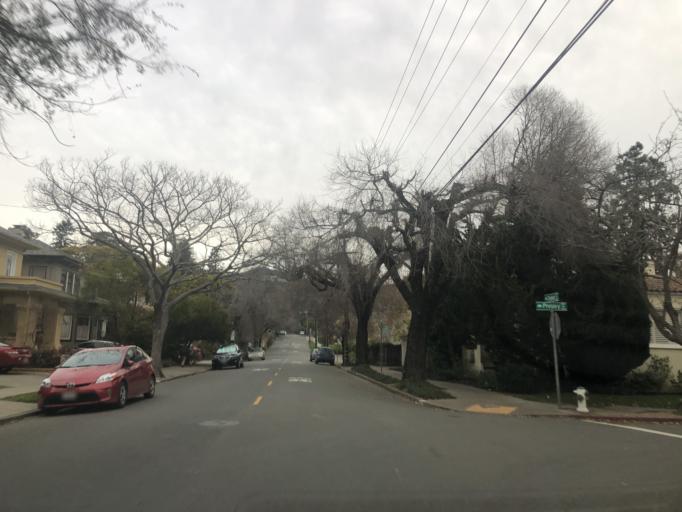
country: US
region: California
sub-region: Alameda County
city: Piedmont
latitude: 37.8485
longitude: -122.2486
